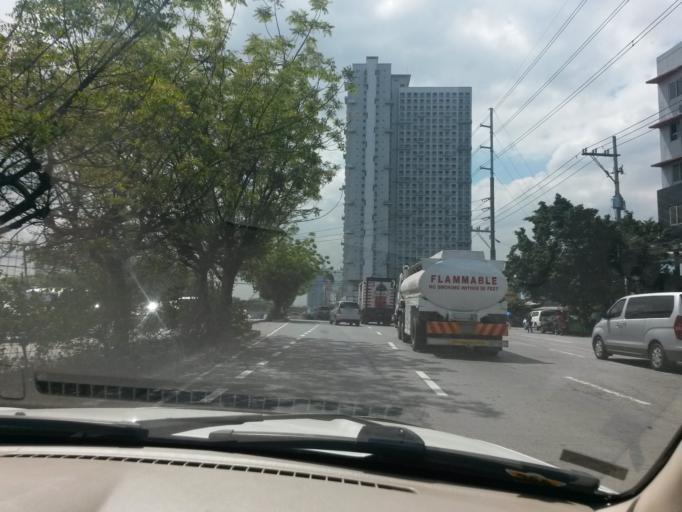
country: PH
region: Metro Manila
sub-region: Quezon City
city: Quezon City
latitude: 14.6470
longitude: 121.0743
